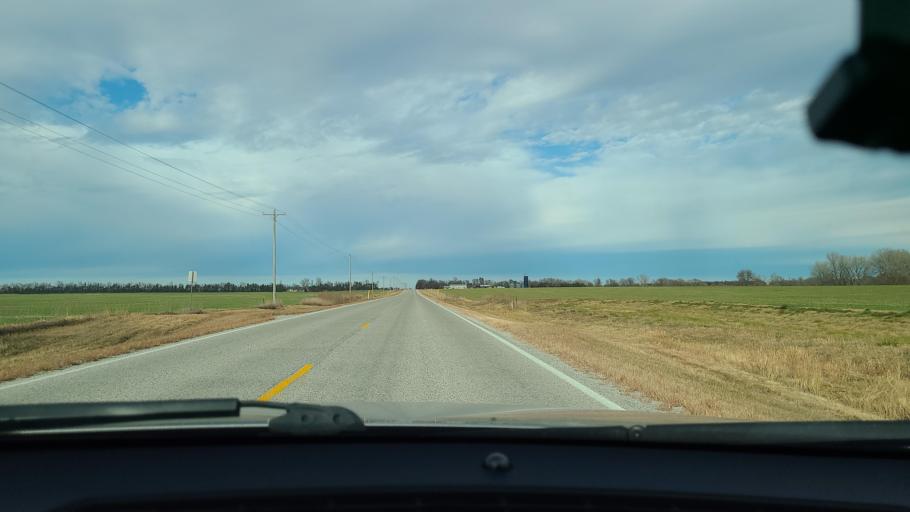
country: US
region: Kansas
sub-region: McPherson County
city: Inman
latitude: 38.3054
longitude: -97.9248
